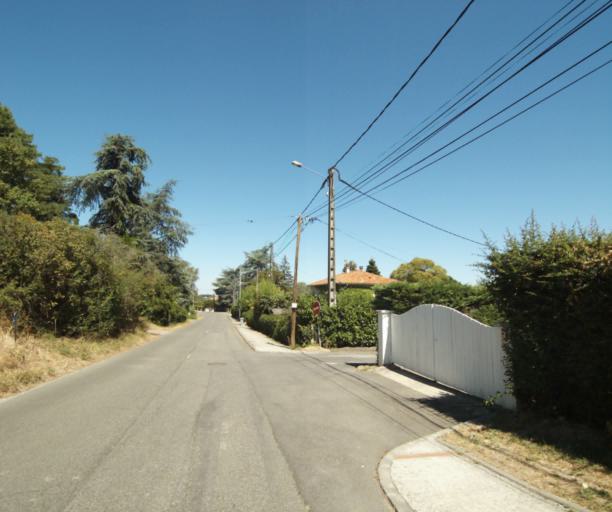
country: FR
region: Midi-Pyrenees
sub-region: Departement de la Haute-Garonne
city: Castanet-Tolosan
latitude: 43.5088
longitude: 1.4984
